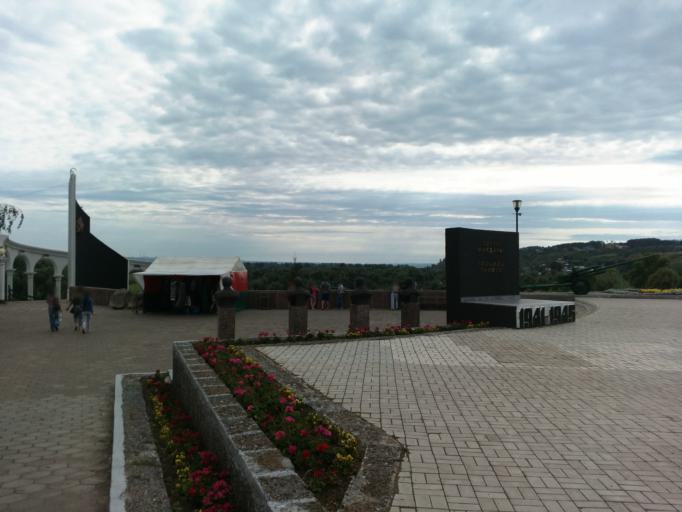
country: RU
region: Tatarstan
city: Yelabuga
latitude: 55.7547
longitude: 52.0537
